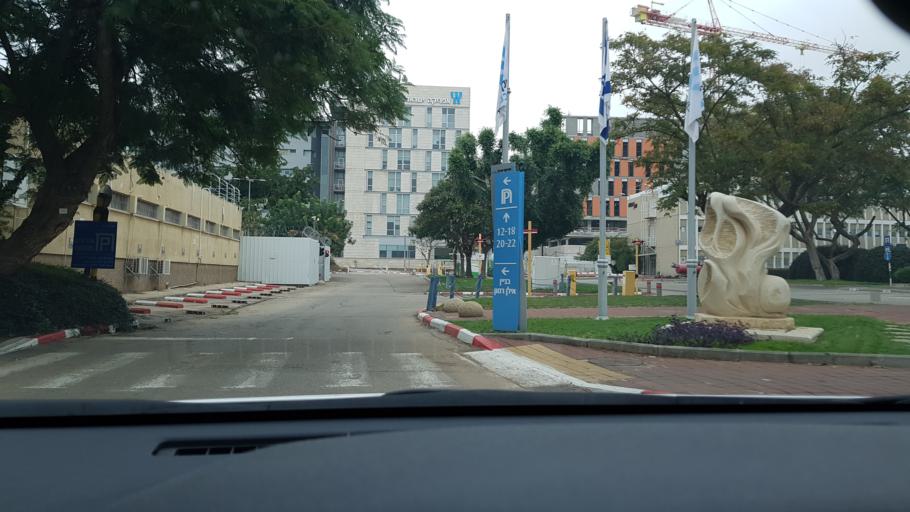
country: IL
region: Central District
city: Ness Ziona
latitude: 31.9163
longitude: 34.8043
